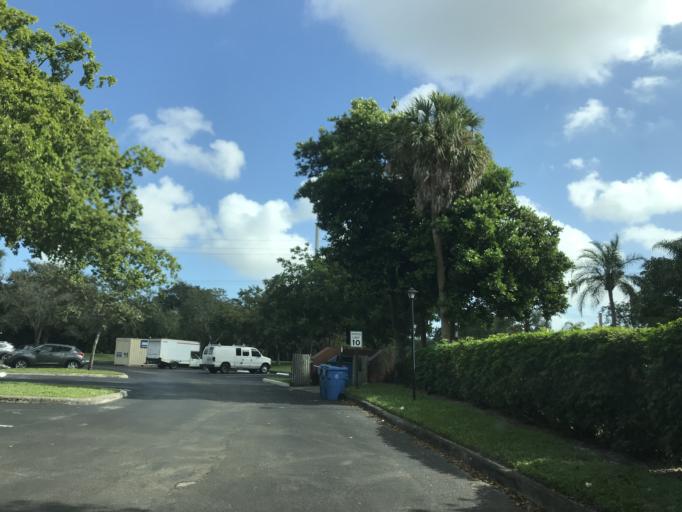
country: US
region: Florida
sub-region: Broward County
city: Coconut Creek
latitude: 26.2691
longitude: -80.1874
